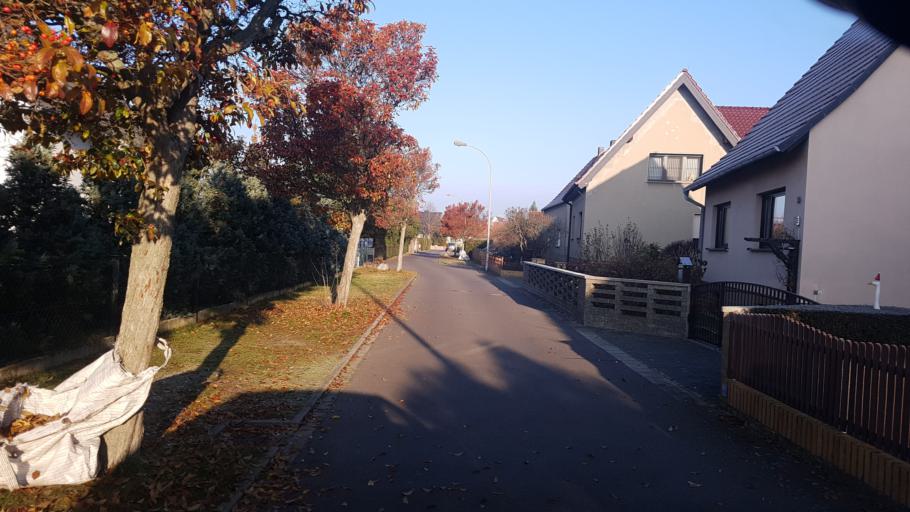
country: DE
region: Brandenburg
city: Tettau
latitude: 51.4309
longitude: 13.7339
